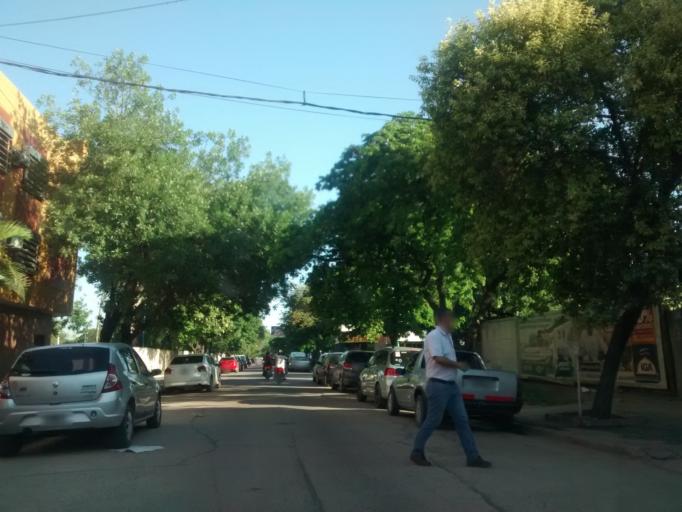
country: AR
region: Chaco
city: Resistencia
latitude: -27.4563
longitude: -58.9824
